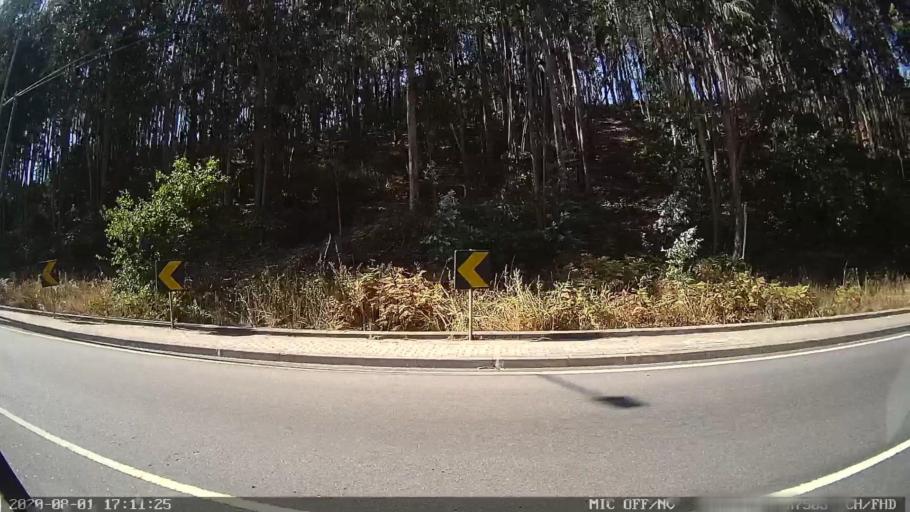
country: PT
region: Porto
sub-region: Trofa
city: Bougado
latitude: 41.3397
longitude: -8.5227
